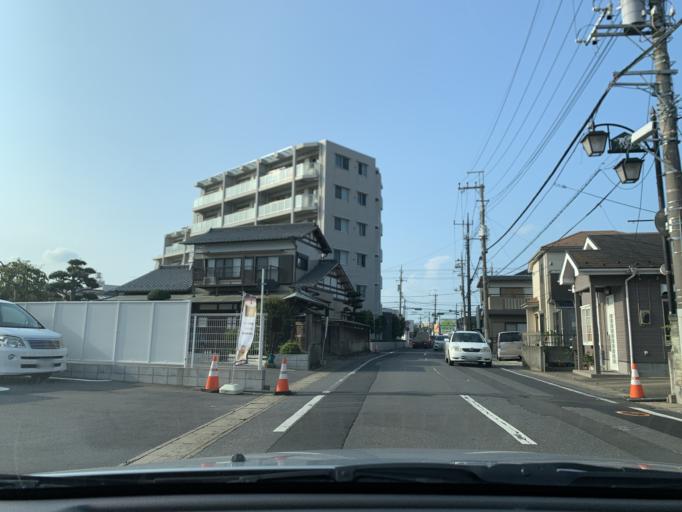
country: JP
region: Chiba
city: Kashiwa
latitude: 35.8661
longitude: 139.9412
